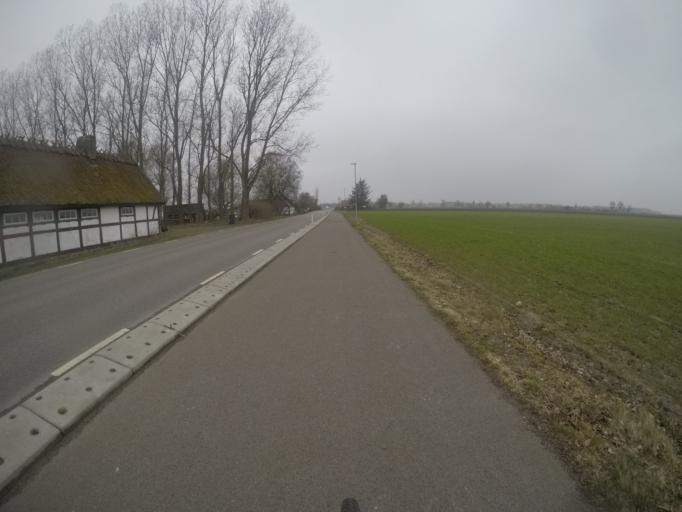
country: SE
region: Skane
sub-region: Helsingborg
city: Odakra
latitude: 56.2156
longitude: 12.6895
